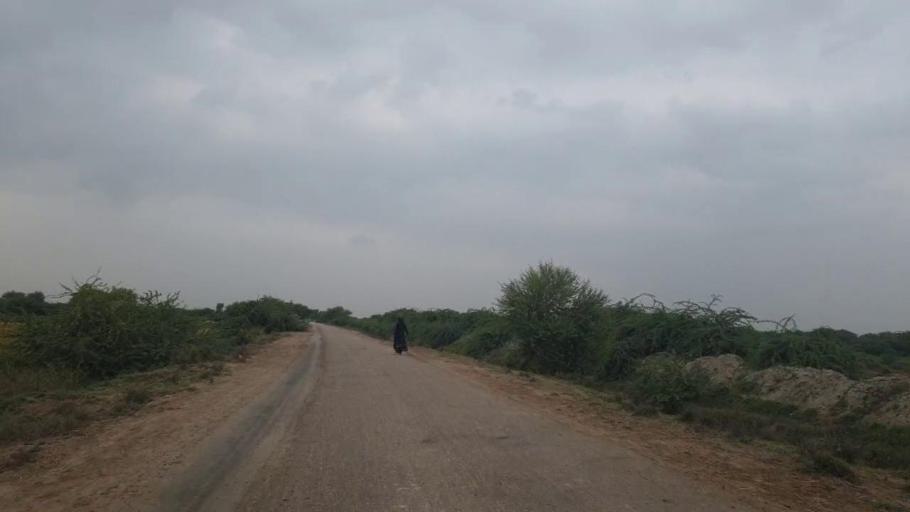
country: PK
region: Sindh
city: Badin
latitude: 24.6363
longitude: 68.6820
